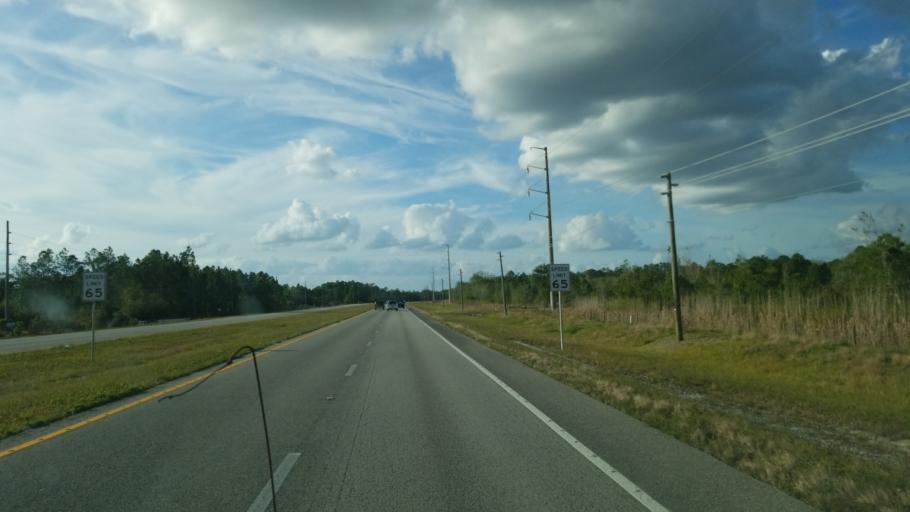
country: US
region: Florida
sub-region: Osceola County
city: Saint Cloud
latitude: 28.1661
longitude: -81.1232
